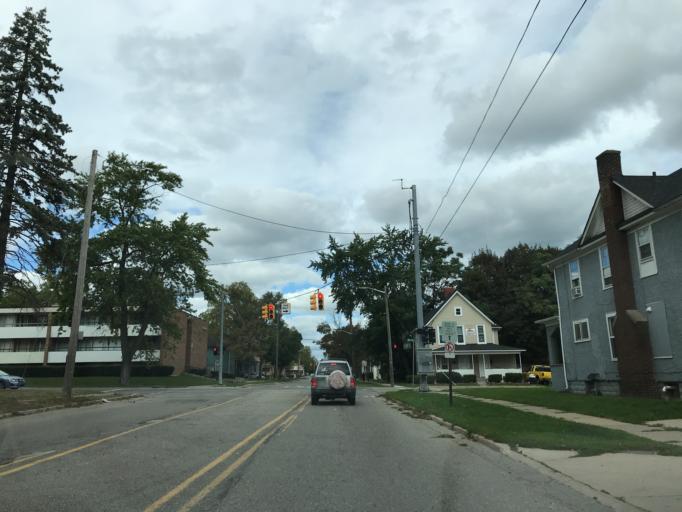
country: US
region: Michigan
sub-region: Washtenaw County
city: Ypsilanti
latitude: 42.2433
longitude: -83.6190
